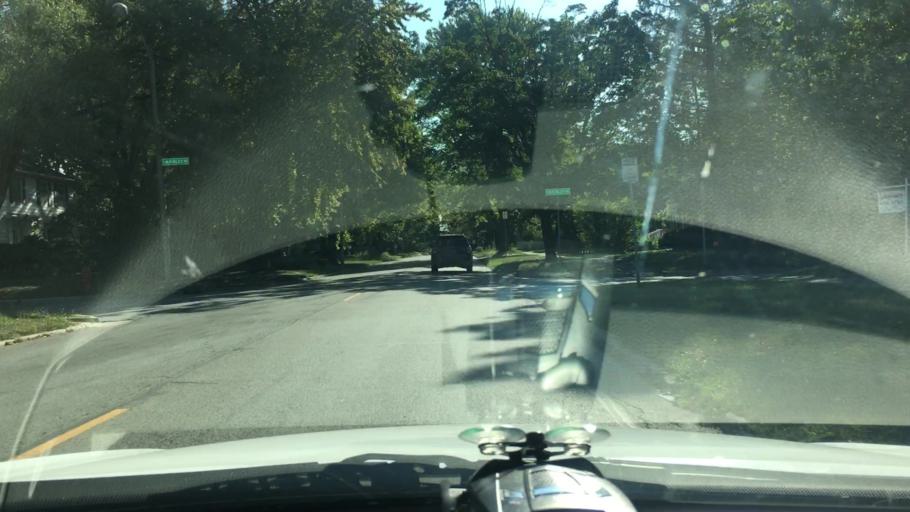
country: US
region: Illinois
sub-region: Champaign County
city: Champaign
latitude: 40.1126
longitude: -88.2628
